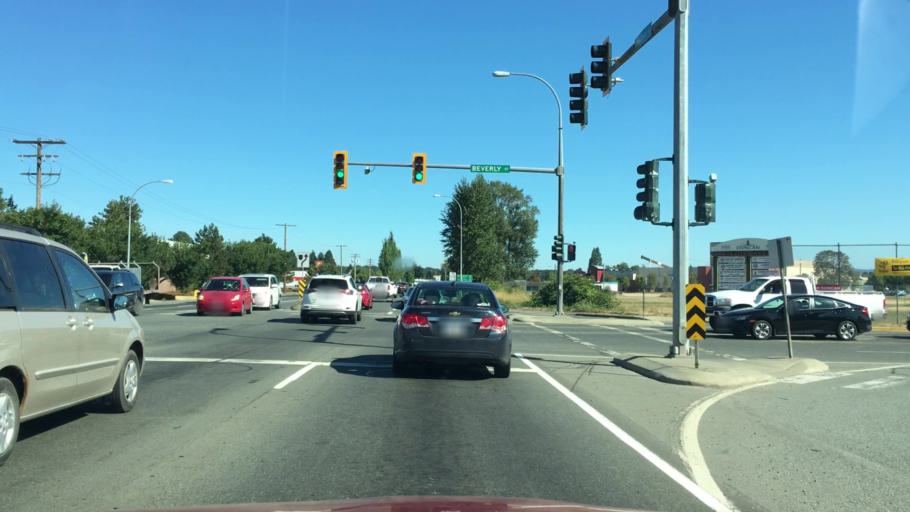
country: CA
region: British Columbia
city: Duncan
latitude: 48.7867
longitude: -123.7065
